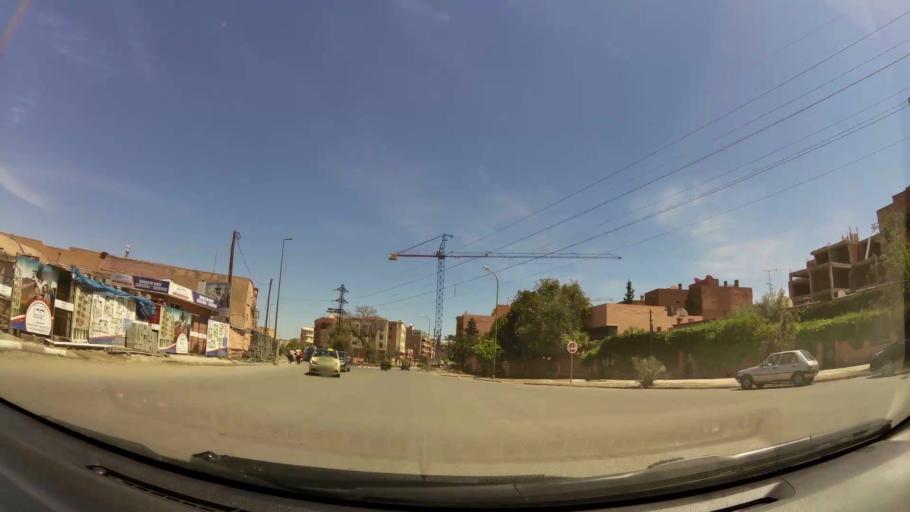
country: MA
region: Marrakech-Tensift-Al Haouz
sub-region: Marrakech
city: Marrakesh
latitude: 31.6264
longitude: -8.0197
